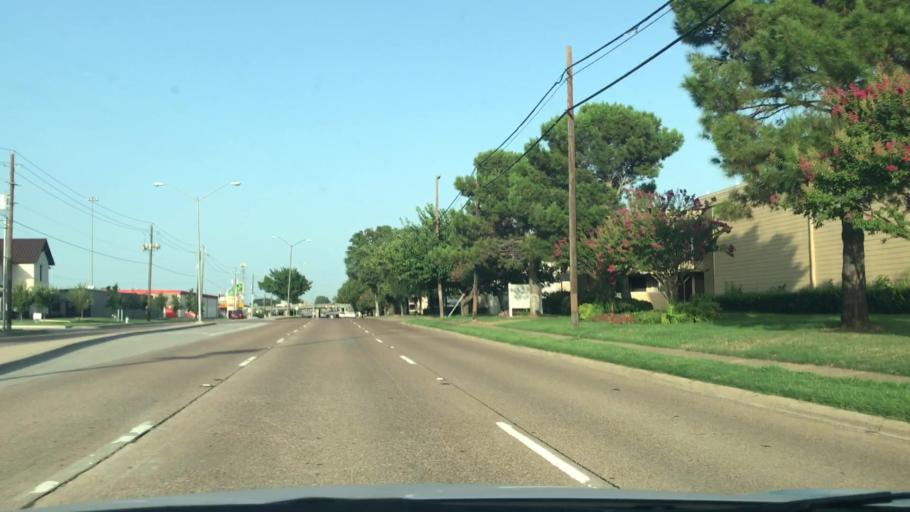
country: US
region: Texas
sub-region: Dallas County
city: Garland
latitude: 32.8787
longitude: -96.6936
